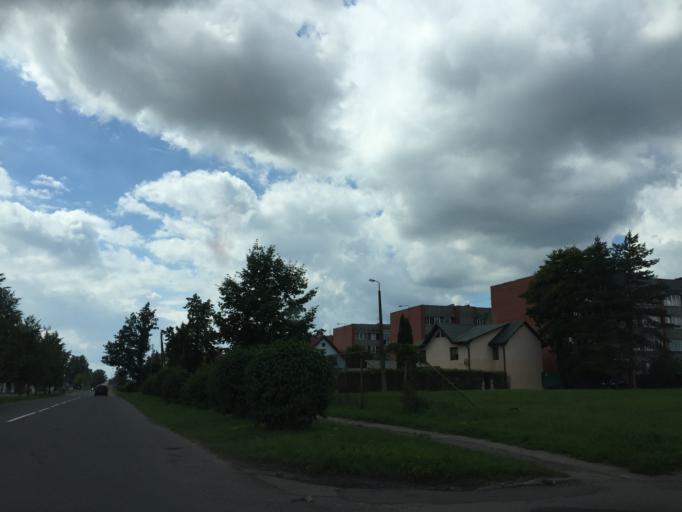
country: LV
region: Ozolnieku
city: Ozolnieki
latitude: 56.6577
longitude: 23.7610
